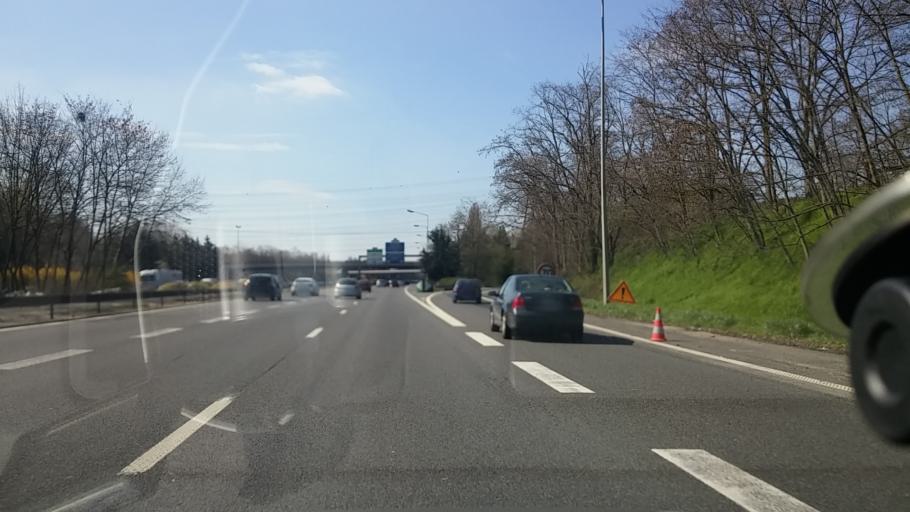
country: FR
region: Ile-de-France
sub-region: Departement de l'Essonne
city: Champlan
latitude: 48.7146
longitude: 2.2728
